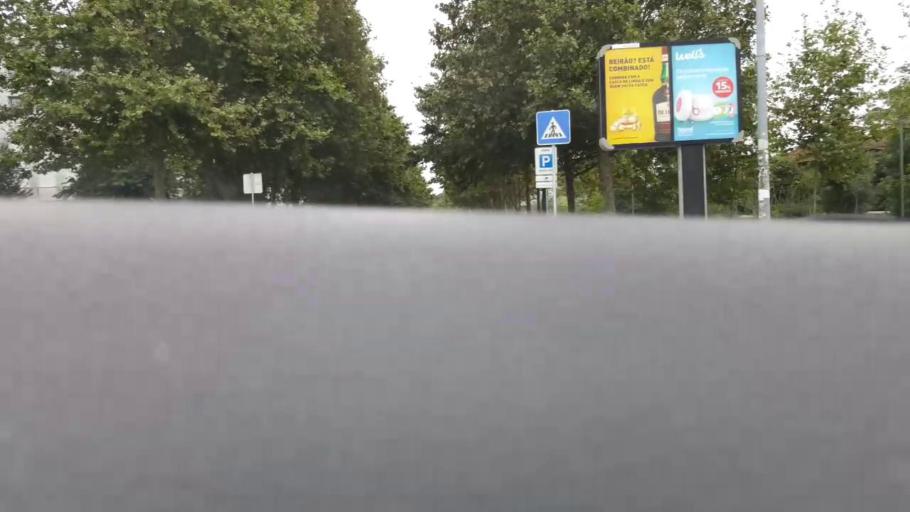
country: PT
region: Porto
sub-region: Maia
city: Pedroucos
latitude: 41.1776
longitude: -8.5983
